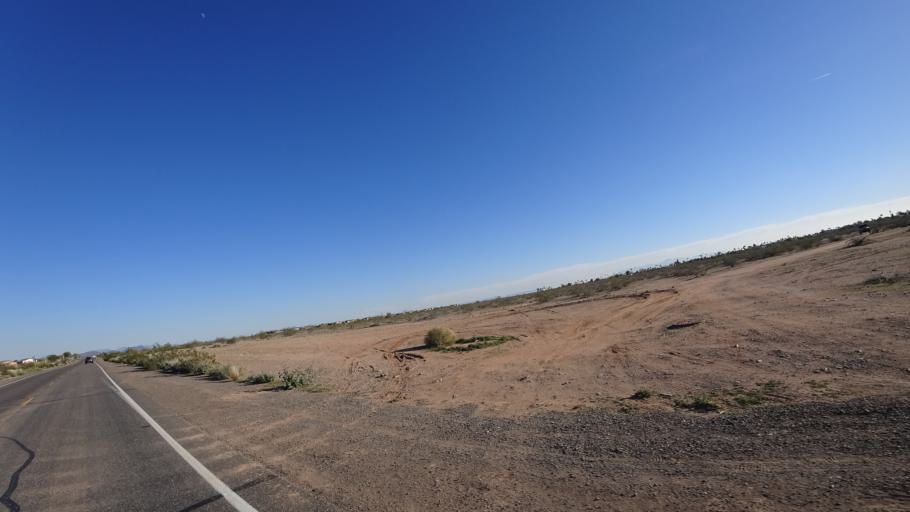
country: US
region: Arizona
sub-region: Maricopa County
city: Sun City West
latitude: 33.6893
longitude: -112.3308
